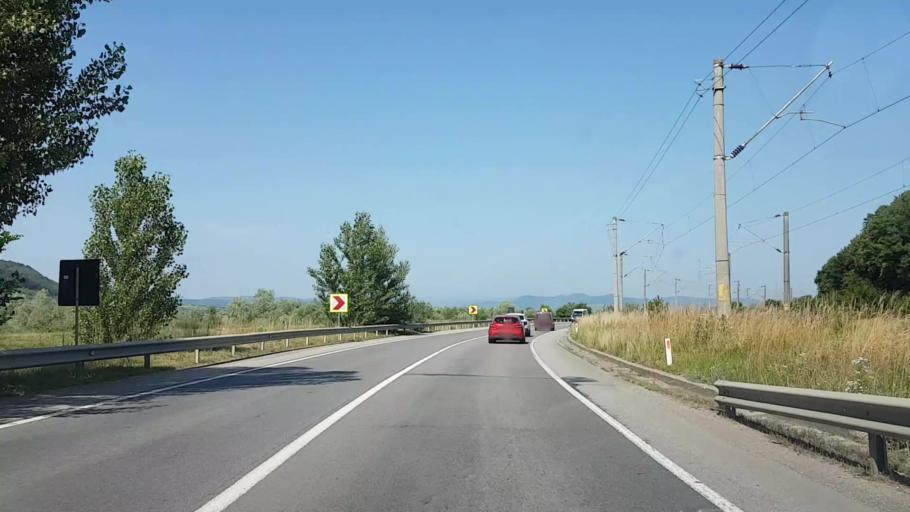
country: RO
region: Bistrita-Nasaud
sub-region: Comuna Beclean
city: Beclean
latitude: 47.1855
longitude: 24.1939
